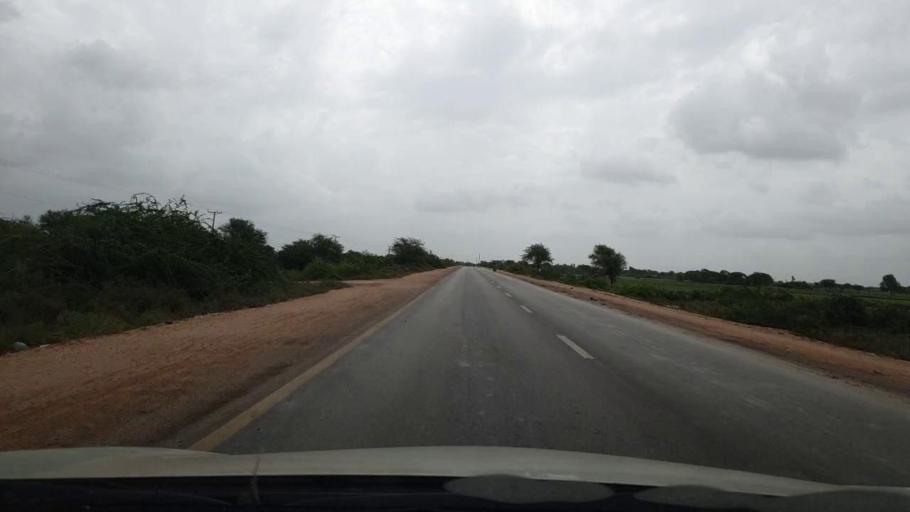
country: PK
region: Sindh
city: Mirpur Batoro
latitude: 24.6236
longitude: 68.3279
